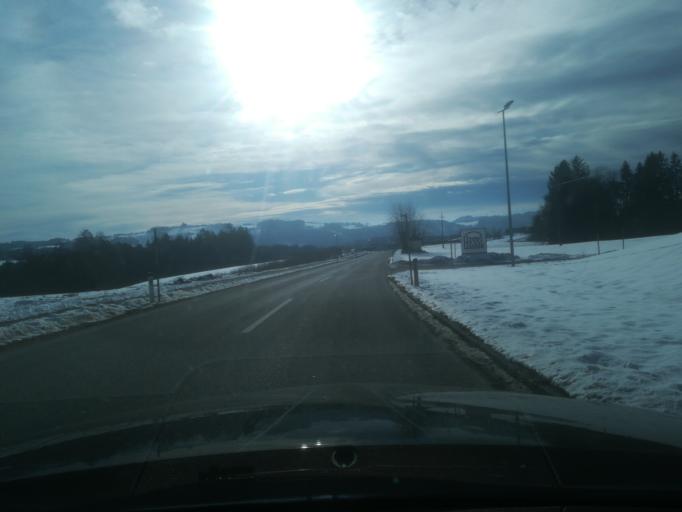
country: AT
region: Upper Austria
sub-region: Politischer Bezirk Perg
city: Perg
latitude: 48.3252
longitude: 14.6236
